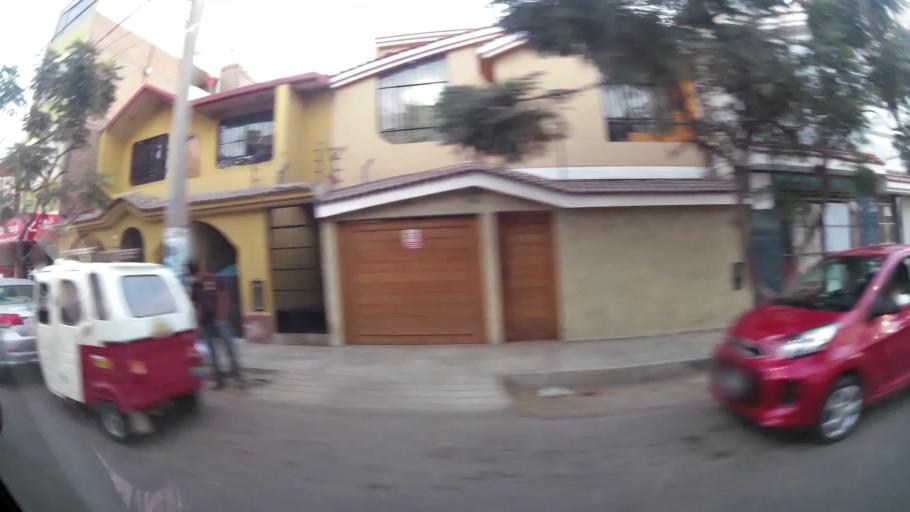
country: PE
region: Ica
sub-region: Provincia de Ica
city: Ica
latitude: -14.0694
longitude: -75.7326
